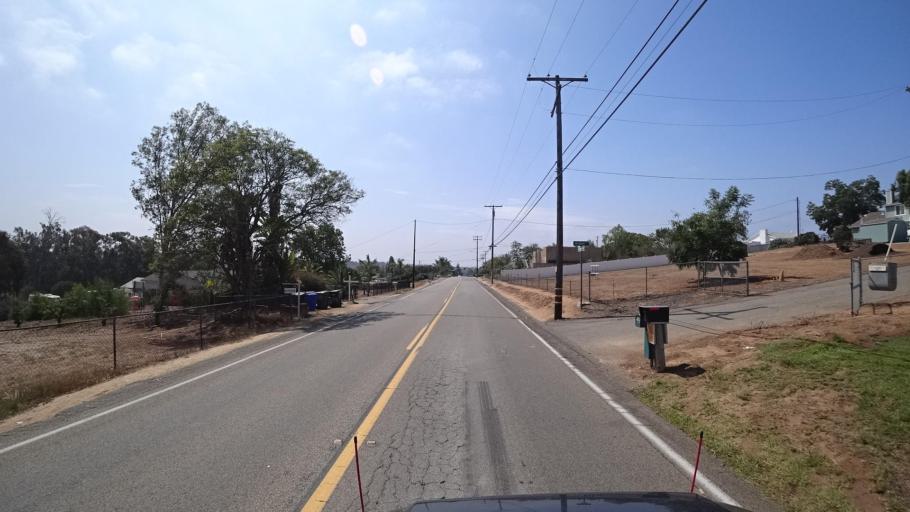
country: US
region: California
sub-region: San Diego County
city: Fallbrook
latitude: 33.3719
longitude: -117.2278
